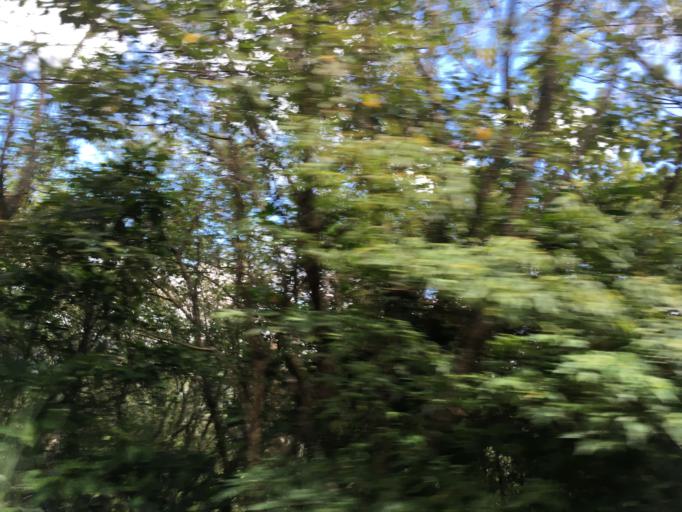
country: TW
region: Taipei
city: Taipei
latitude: 24.9371
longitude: 121.5807
